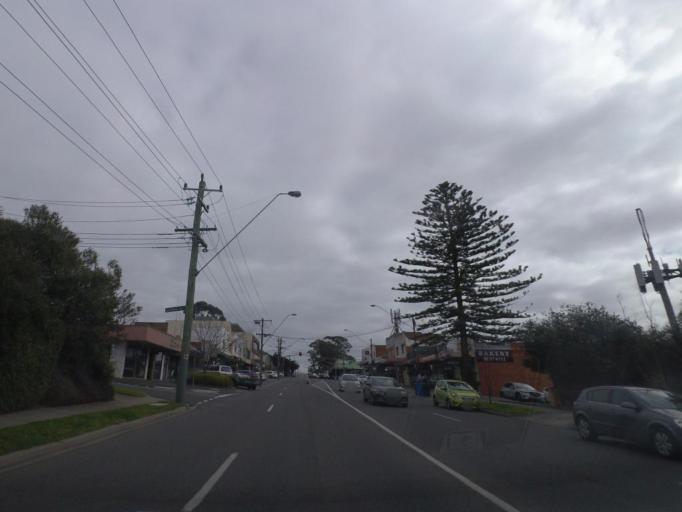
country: AU
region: Victoria
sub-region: Boroondara
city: Balwyn North
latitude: -37.8037
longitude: 145.0846
